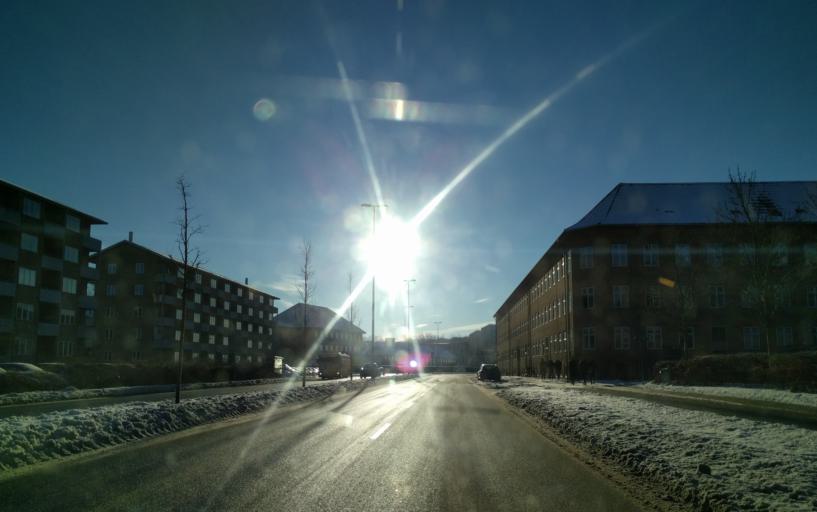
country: DK
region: North Denmark
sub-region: Alborg Kommune
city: Aalborg
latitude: 57.0409
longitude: 9.9312
